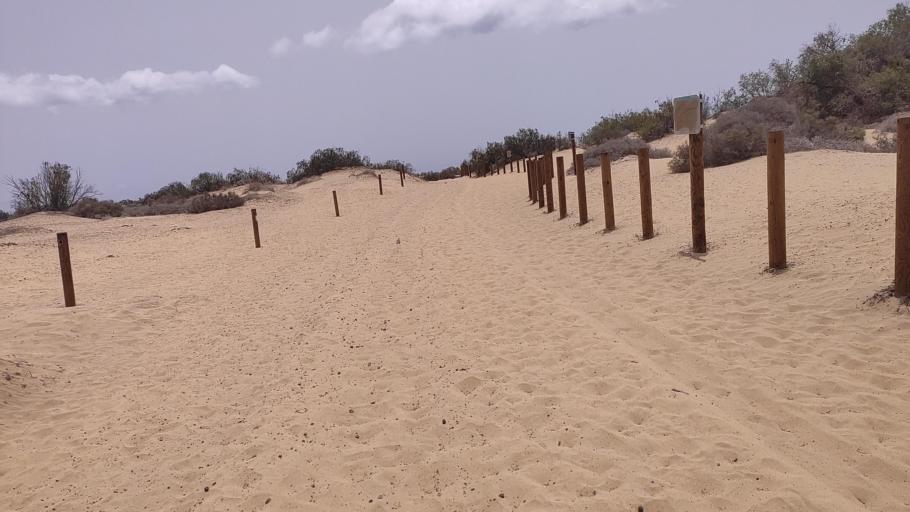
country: ES
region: Canary Islands
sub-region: Provincia de Las Palmas
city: Maspalomas
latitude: 27.7445
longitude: -15.5920
